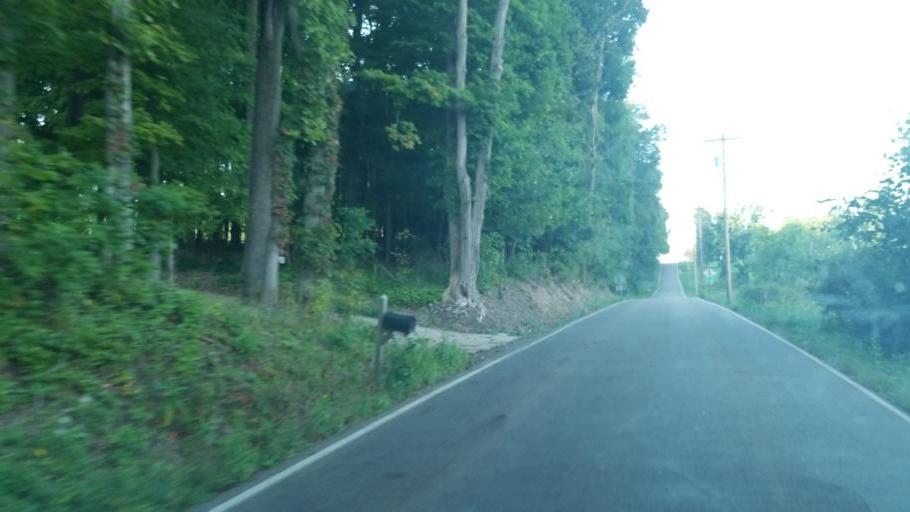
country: US
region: Ohio
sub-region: Knox County
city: Gambier
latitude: 40.3920
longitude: -82.4379
